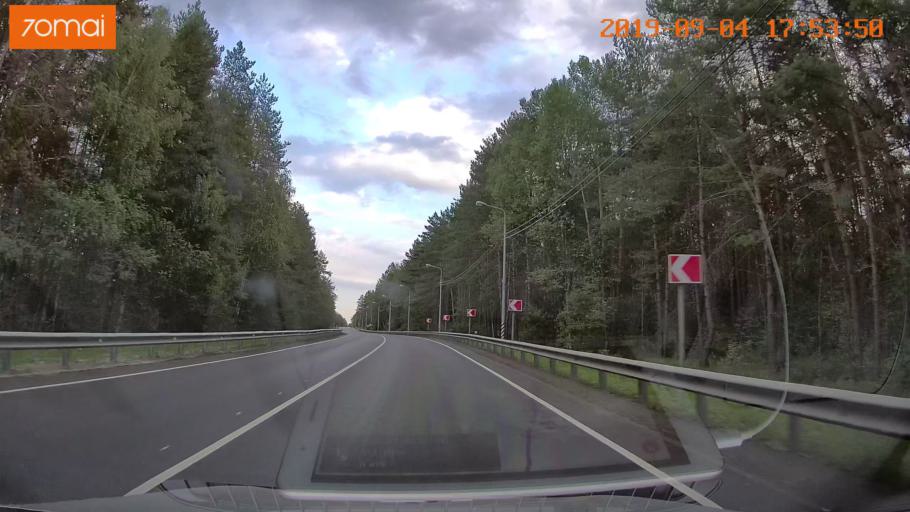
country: RU
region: Moskovskaya
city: Imeni Tsyurupy
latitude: 55.5139
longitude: 38.7298
